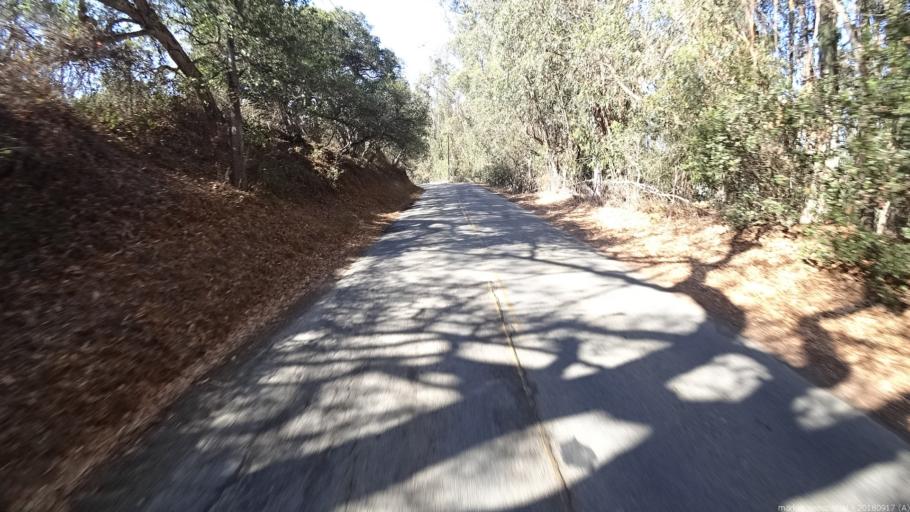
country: US
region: California
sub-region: Monterey County
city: Elkhorn
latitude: 36.8224
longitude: -121.7294
